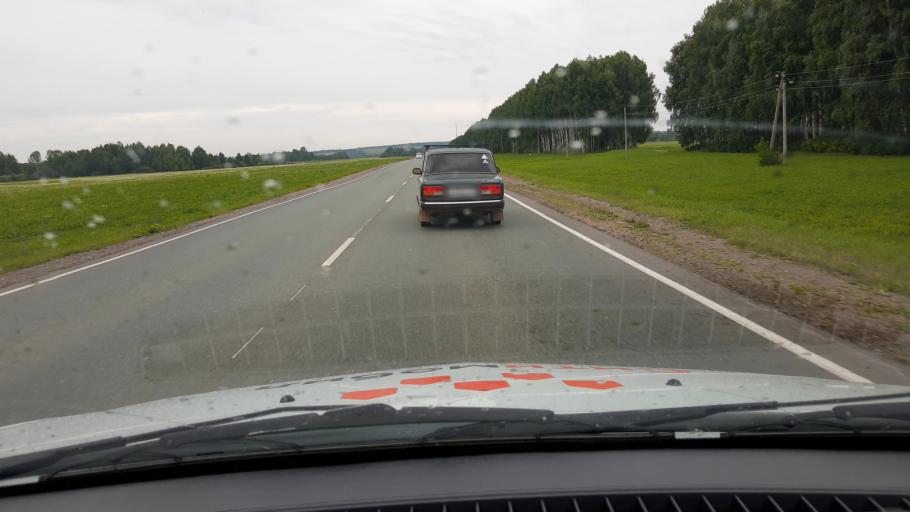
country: RU
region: Bashkortostan
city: Krasnaya Gorka
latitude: 55.1373
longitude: 56.6643
